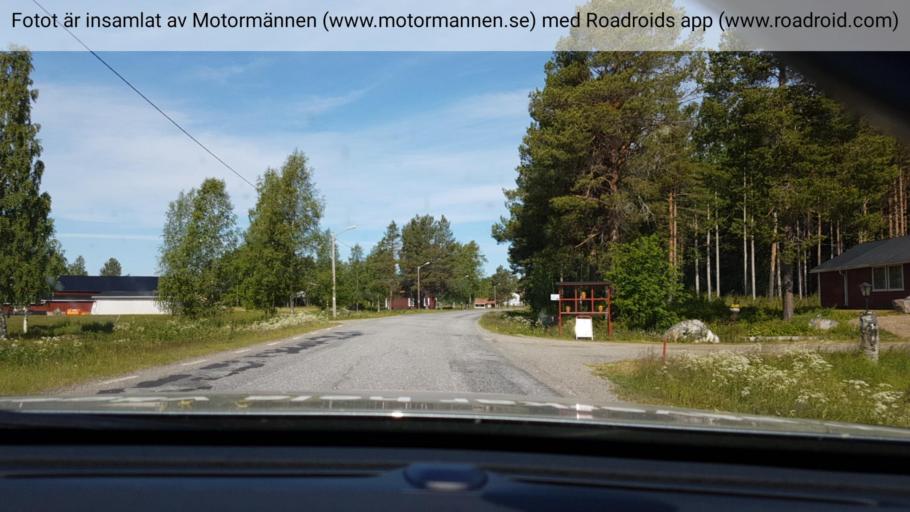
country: SE
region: Vaesterbotten
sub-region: Dorotea Kommun
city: Dorotea
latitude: 64.3912
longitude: 16.0798
